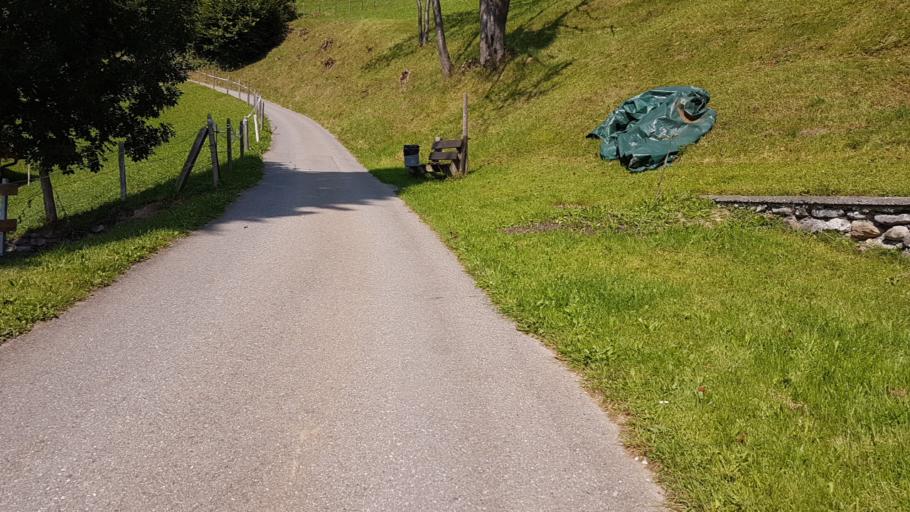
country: CH
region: Bern
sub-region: Frutigen-Niedersimmental District
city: Aeschi
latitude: 46.5904
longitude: 7.7233
